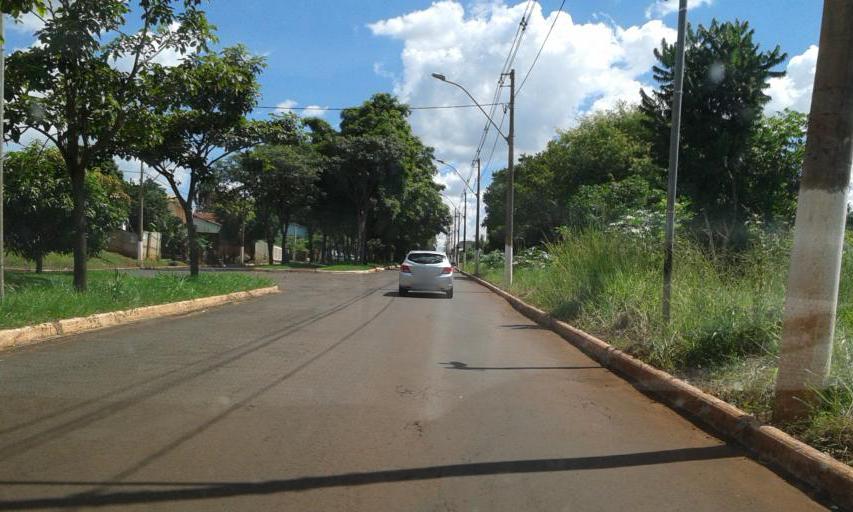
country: BR
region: Minas Gerais
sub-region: Ituiutaba
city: Ituiutaba
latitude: -18.9676
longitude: -49.4736
